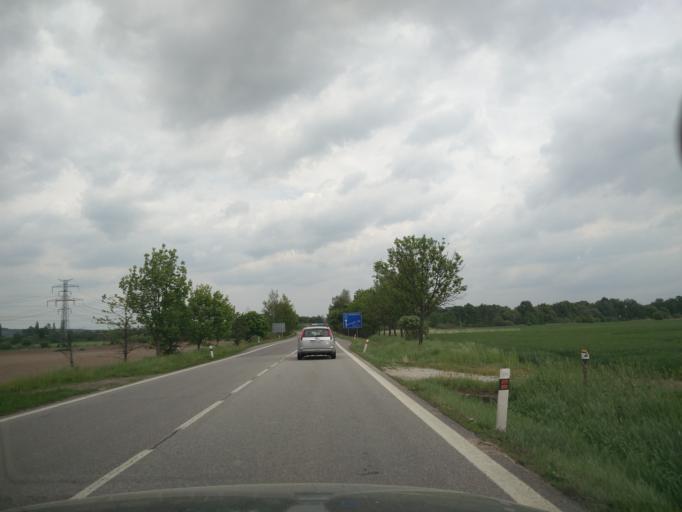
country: CZ
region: Jihocesky
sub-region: Okres Ceske Budejovice
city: Hluboka nad Vltavou
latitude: 49.0169
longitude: 14.4276
